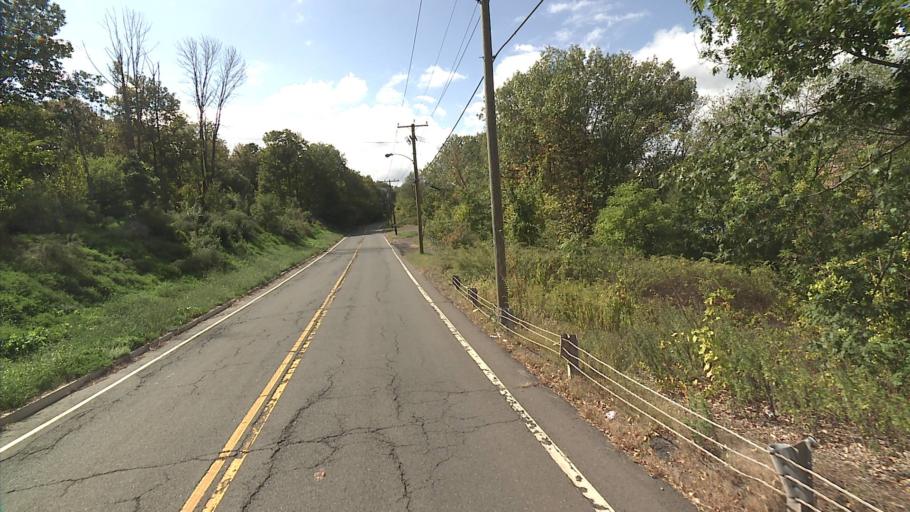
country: US
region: Connecticut
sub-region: Middlesex County
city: Middletown
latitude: 41.5490
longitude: -72.6761
